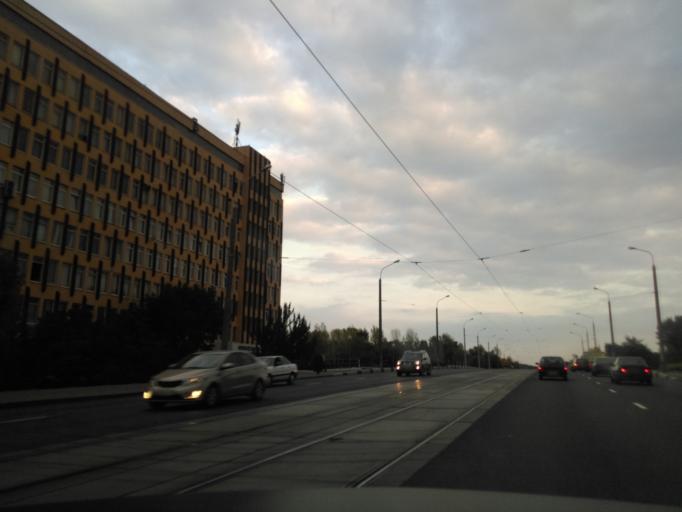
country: BY
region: Minsk
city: Minsk
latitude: 53.8942
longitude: 27.6096
